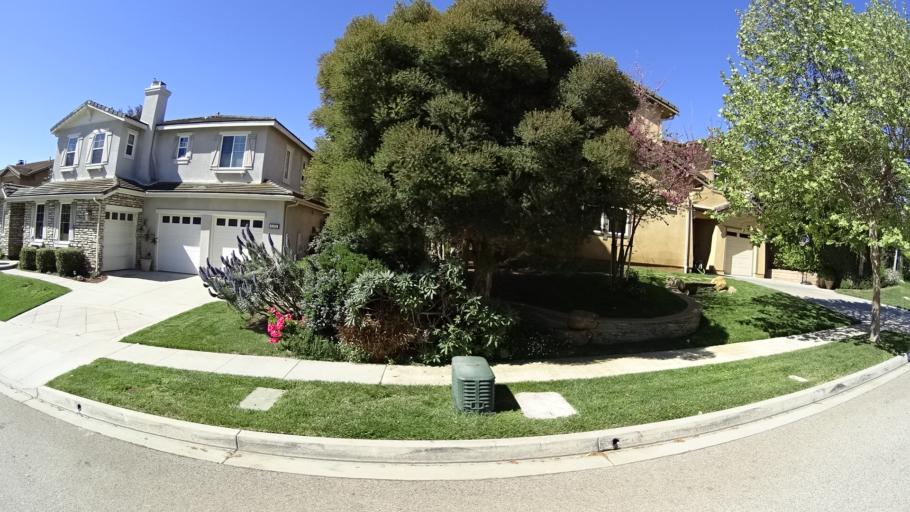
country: US
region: California
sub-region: Ventura County
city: Casa Conejo
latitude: 34.1785
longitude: -118.9882
